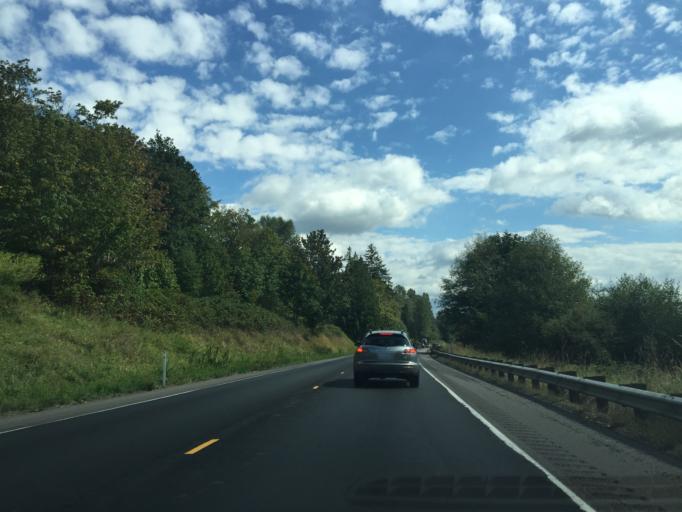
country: US
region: Washington
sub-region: Snohomish County
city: Snohomish
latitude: 47.9098
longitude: -122.0509
